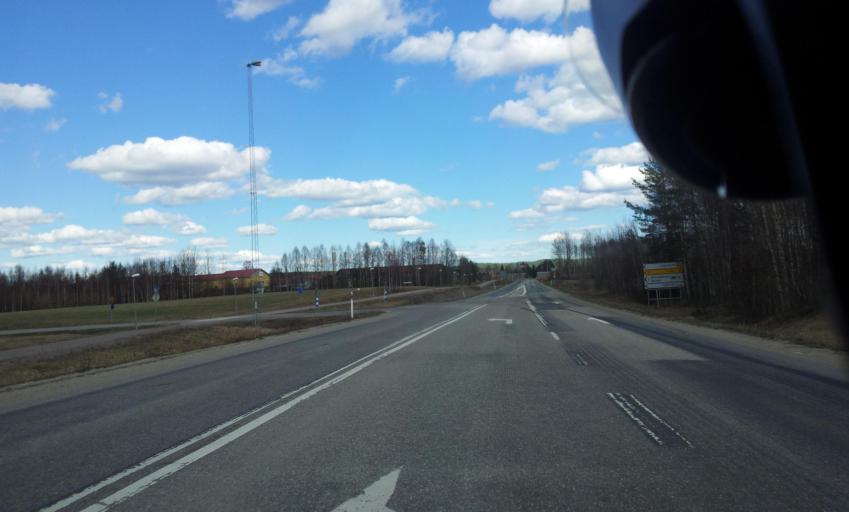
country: SE
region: Gaevleborg
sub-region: Ovanakers Kommun
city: Edsbyn
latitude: 61.3677
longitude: 15.8190
